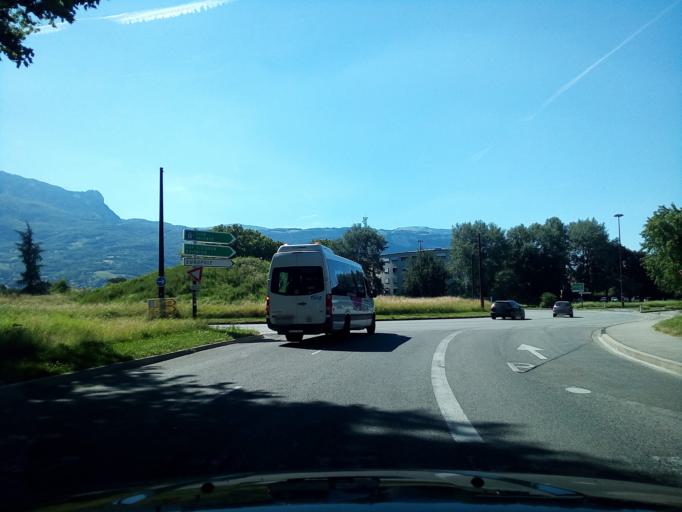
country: FR
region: Rhone-Alpes
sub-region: Departement de l'Isere
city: Grenoble
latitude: 45.1601
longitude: 5.7213
